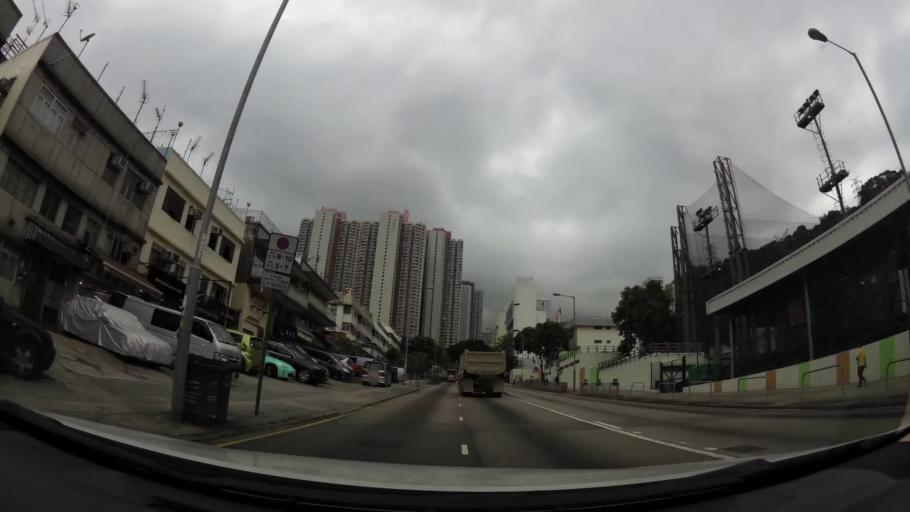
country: HK
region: Tsuen Wan
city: Tsuen Wan
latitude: 22.3738
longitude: 114.1364
